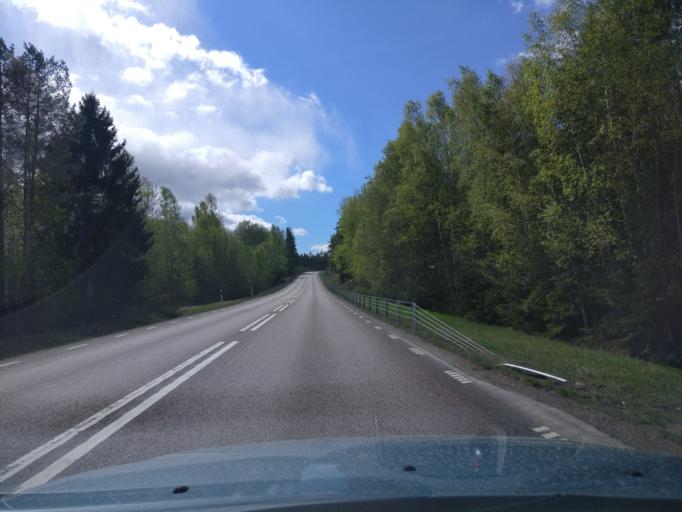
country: SE
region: Vaermland
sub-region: Karlstads Kommun
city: Molkom
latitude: 59.5884
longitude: 13.6868
